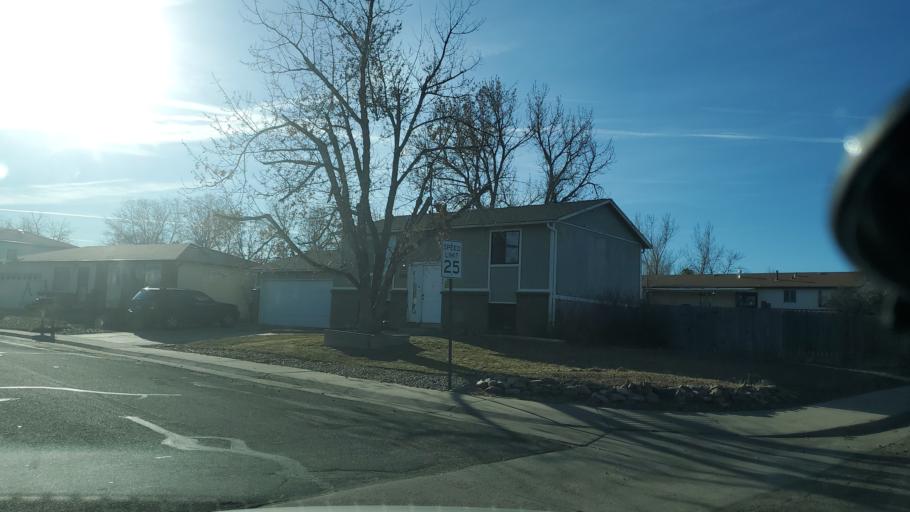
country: US
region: Colorado
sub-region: Adams County
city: Northglenn
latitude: 39.9114
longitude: -104.9460
